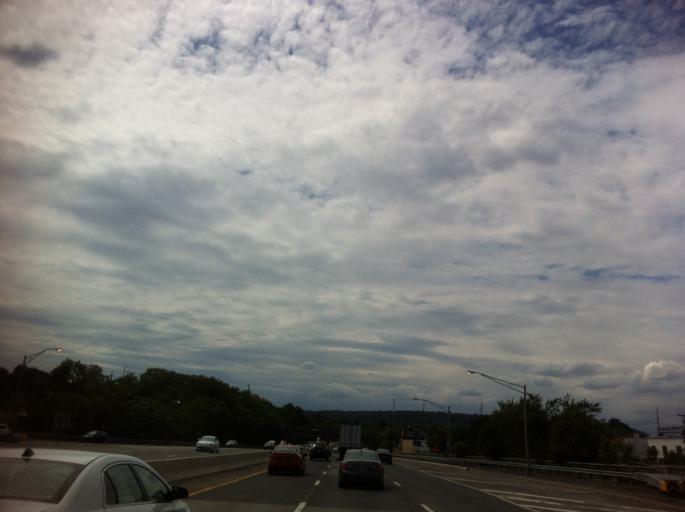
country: US
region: New Jersey
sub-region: Bergen County
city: Elmwood Park
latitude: 40.9017
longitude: -74.1243
